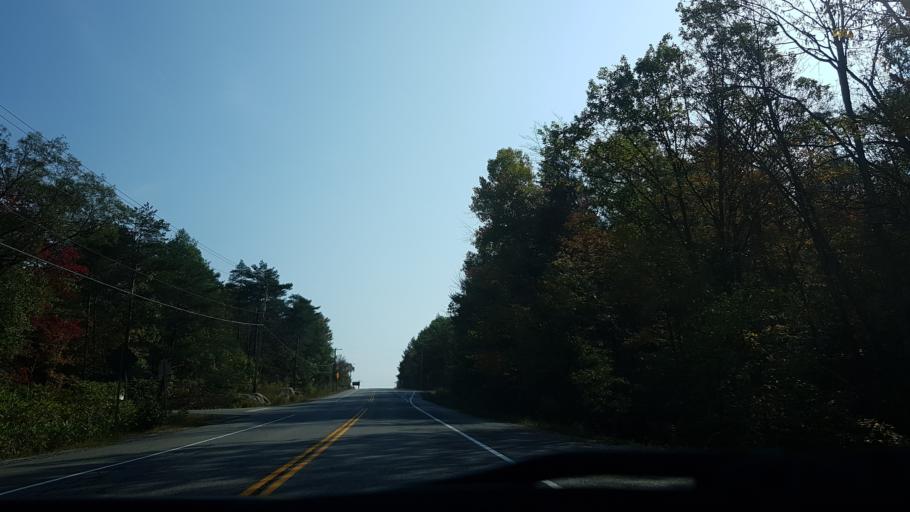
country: CA
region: Ontario
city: Bracebridge
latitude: 44.9834
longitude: -79.2646
